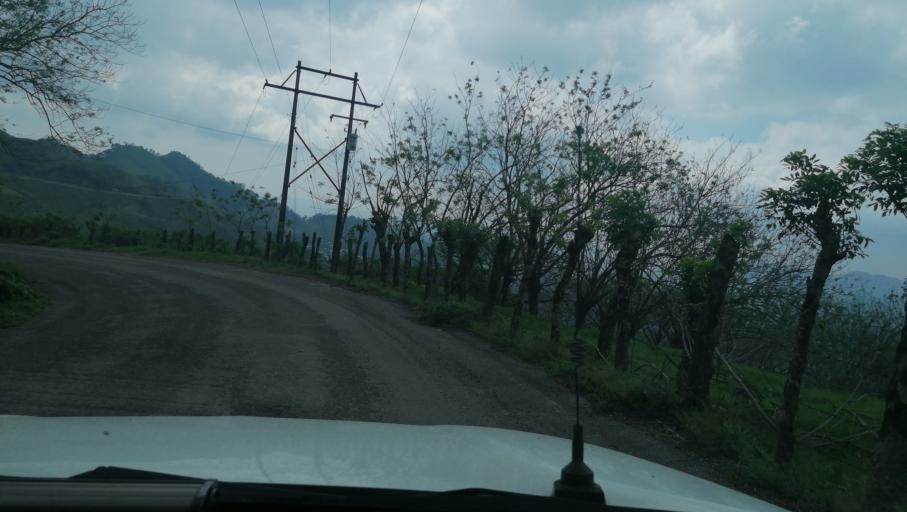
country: MX
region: Chiapas
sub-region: Francisco Leon
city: San Miguel la Sardina
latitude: 17.2427
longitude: -93.2989
